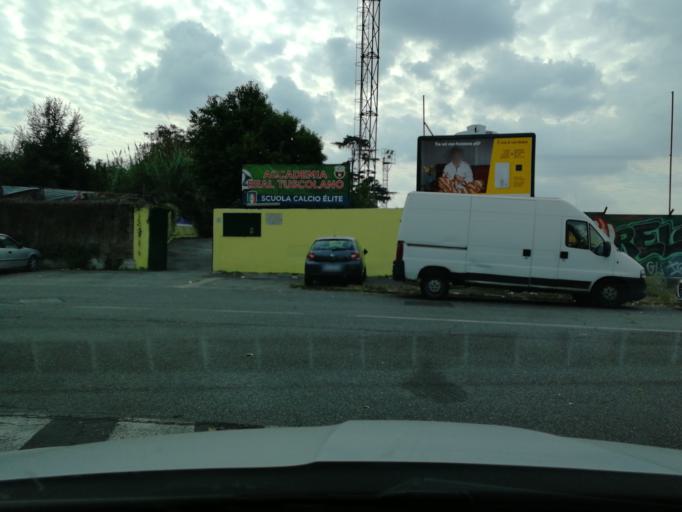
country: IT
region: Latium
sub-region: Citta metropolitana di Roma Capitale
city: Rome
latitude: 41.8581
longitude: 12.5492
